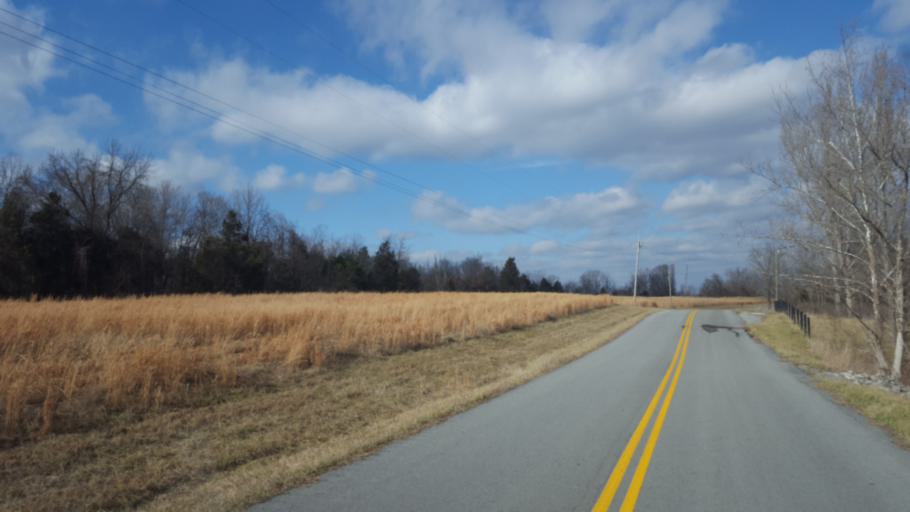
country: US
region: Kentucky
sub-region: Franklin County
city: Frankfort
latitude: 38.3701
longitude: -84.9436
